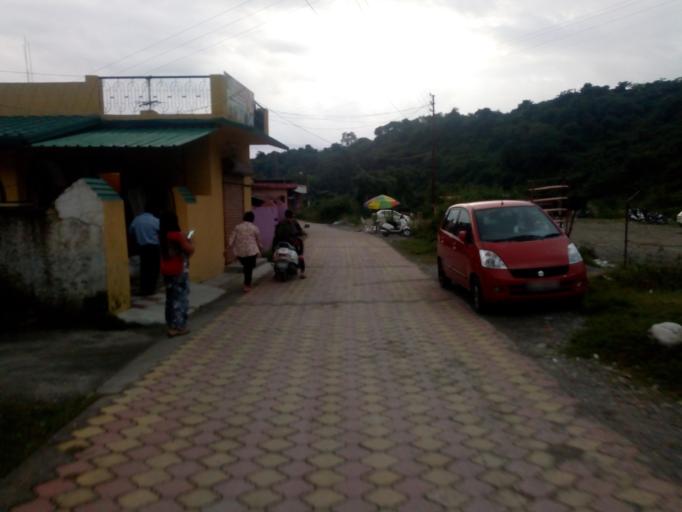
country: IN
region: Uttarakhand
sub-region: Dehradun
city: Dehradun
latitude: 30.3748
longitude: 78.0588
